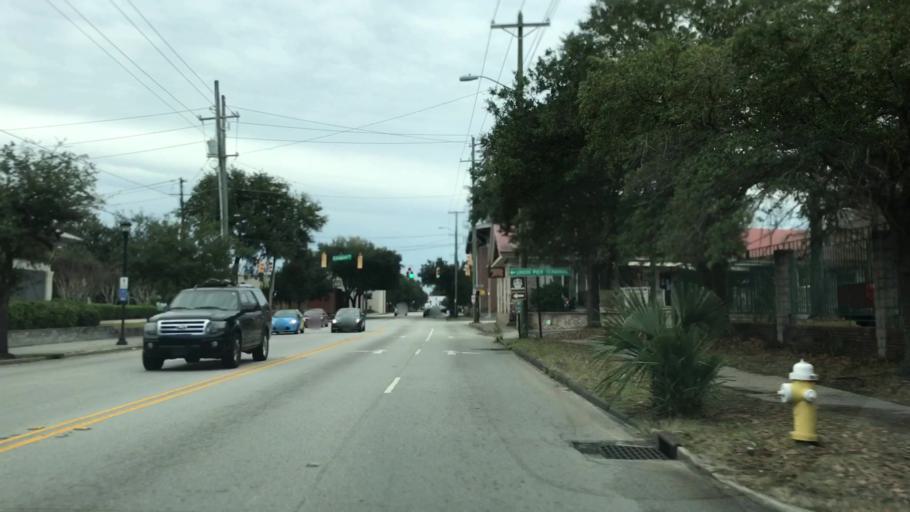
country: US
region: South Carolina
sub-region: Charleston County
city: Charleston
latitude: 32.7926
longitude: -79.9315
